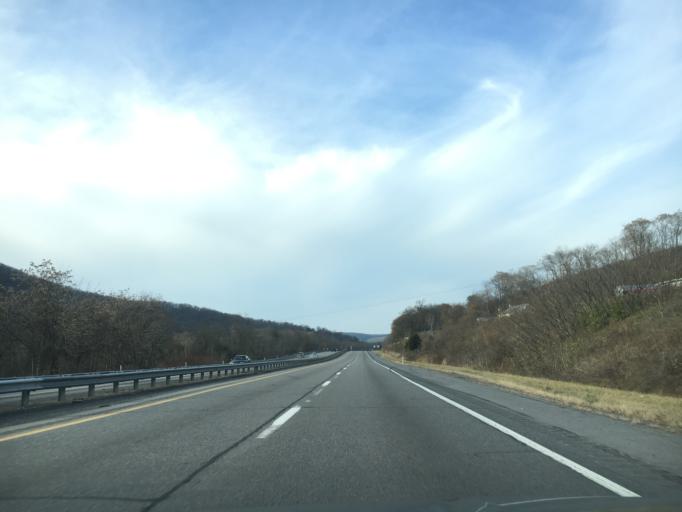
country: US
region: Pennsylvania
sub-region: Montour County
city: Danville
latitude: 40.9751
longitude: -76.6201
